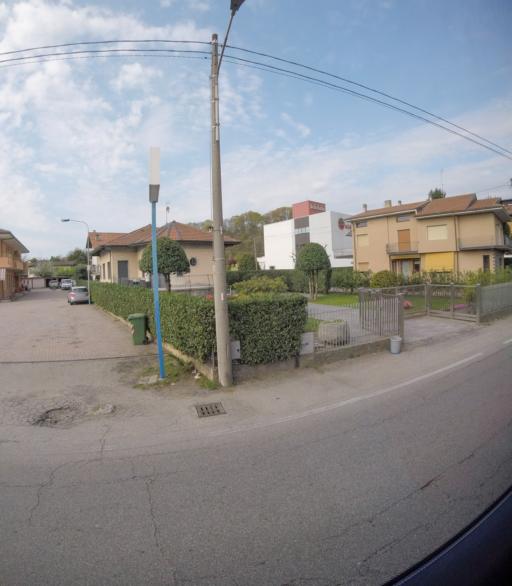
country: IT
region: Piedmont
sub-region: Provincia di Novara
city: Gozzano
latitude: 45.7434
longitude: 8.4340
